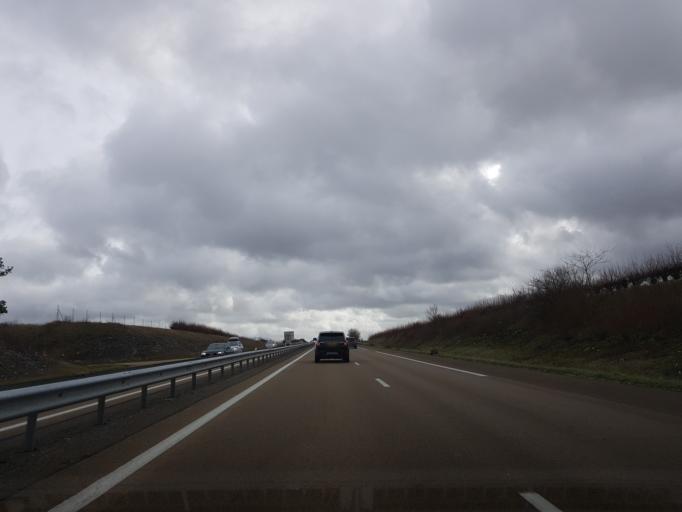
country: FR
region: Champagne-Ardenne
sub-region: Departement de la Haute-Marne
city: Chamarandes-Choignes
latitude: 47.9776
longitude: 5.1356
